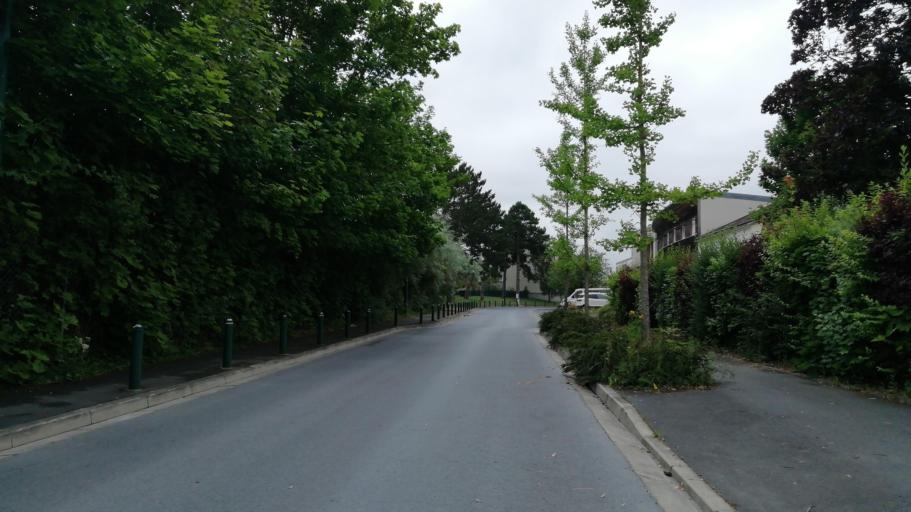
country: FR
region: Champagne-Ardenne
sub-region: Departement de la Marne
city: Betheny
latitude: 49.2545
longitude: 4.0658
